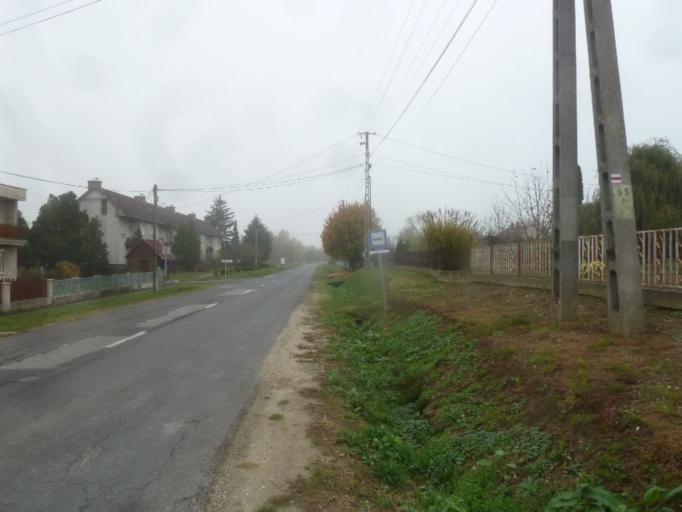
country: HU
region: Zala
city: Nagykanizsa
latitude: 46.5426
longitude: 16.9853
